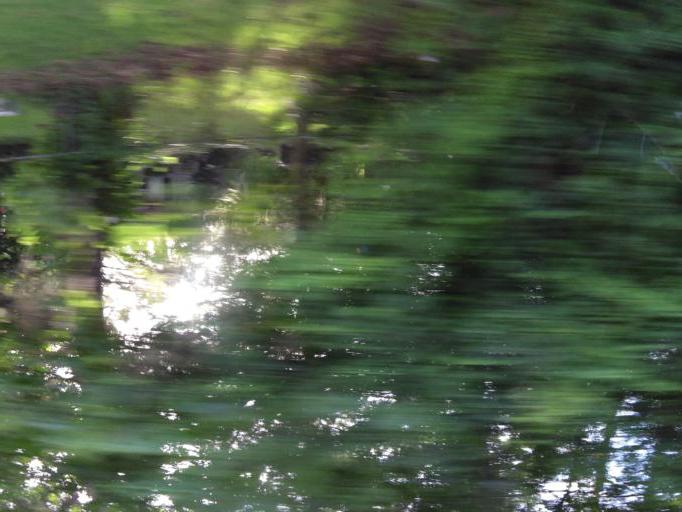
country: US
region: Florida
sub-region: Duval County
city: Jacksonville
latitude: 30.4144
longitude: -81.7322
